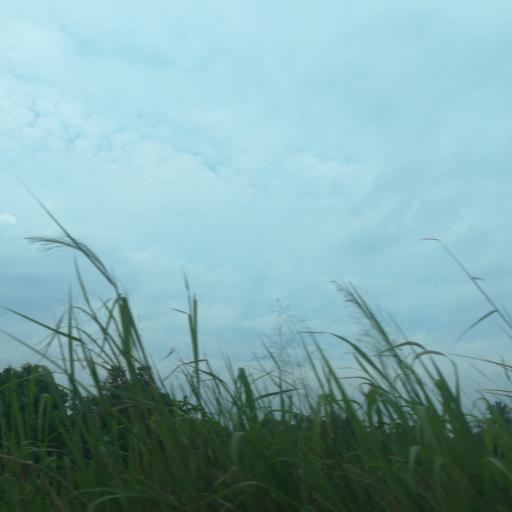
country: NG
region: Lagos
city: Ejirin
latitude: 6.6468
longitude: 3.7582
